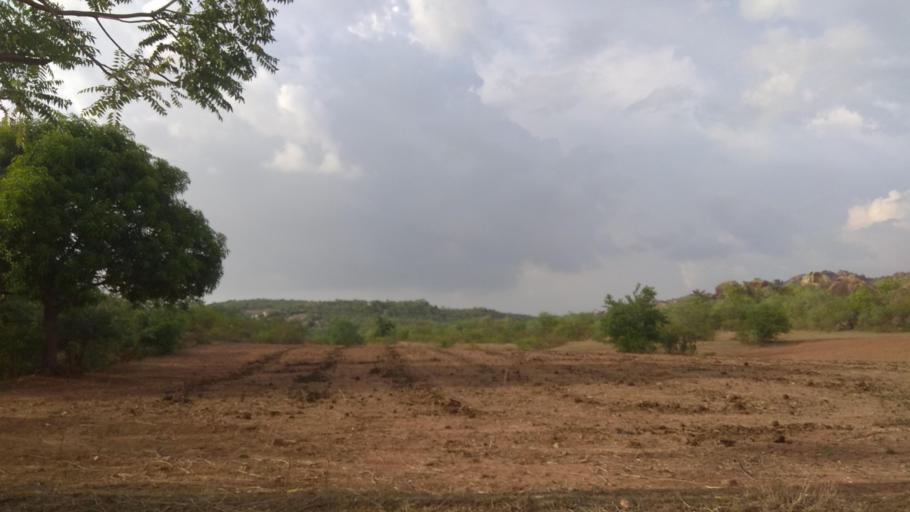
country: IN
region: Telangana
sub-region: Mahbubnagar
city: Farrukhnagar
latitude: 16.8880
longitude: 78.4833
